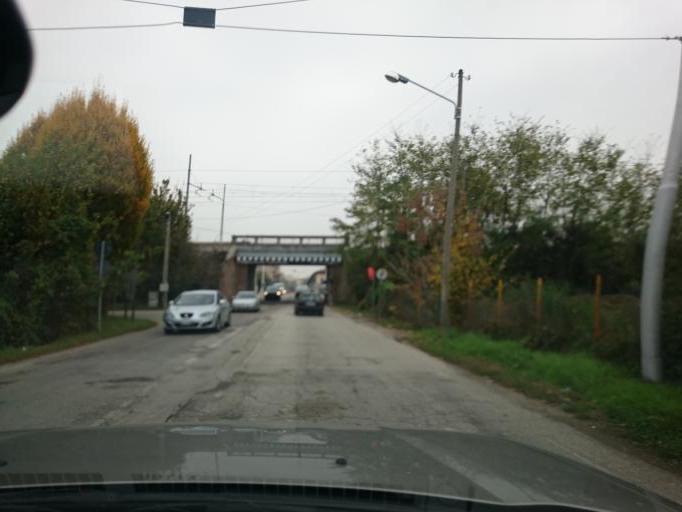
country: IT
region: Veneto
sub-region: Provincia di Padova
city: Padova
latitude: 45.4194
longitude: 11.8614
